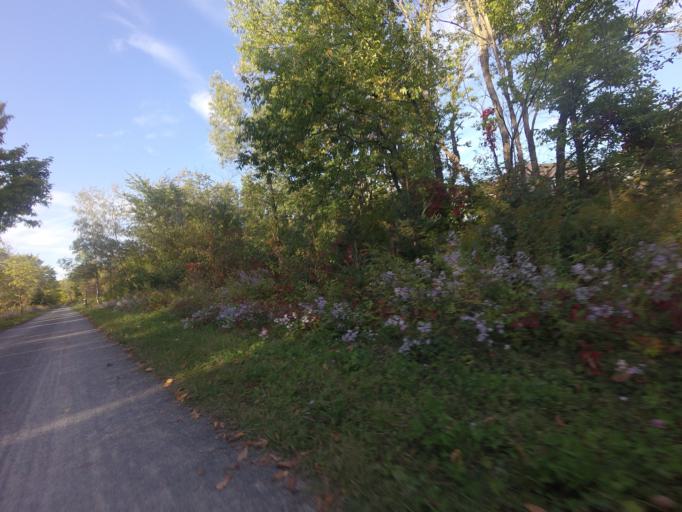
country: CA
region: Quebec
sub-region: Laurentides
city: Prevost
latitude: 45.8430
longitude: -74.0598
